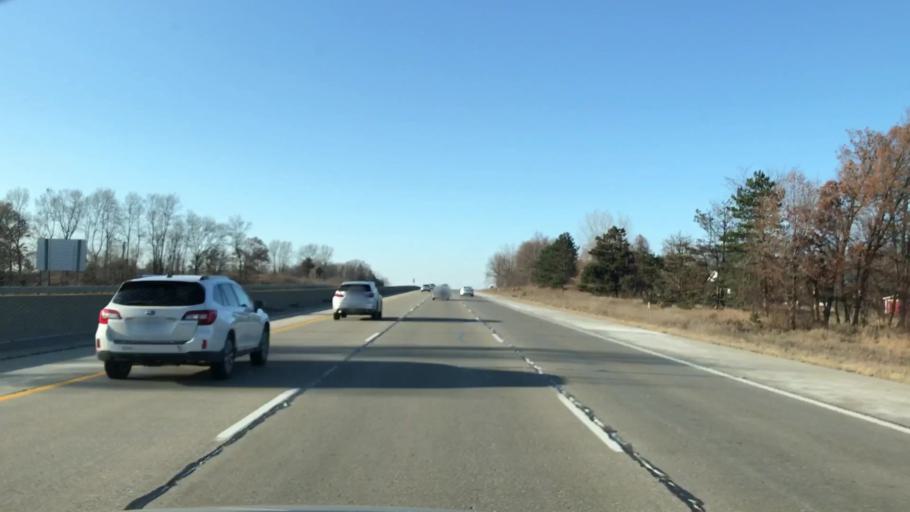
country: US
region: Michigan
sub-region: Livingston County
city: Brighton
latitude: 42.5557
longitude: -83.8181
